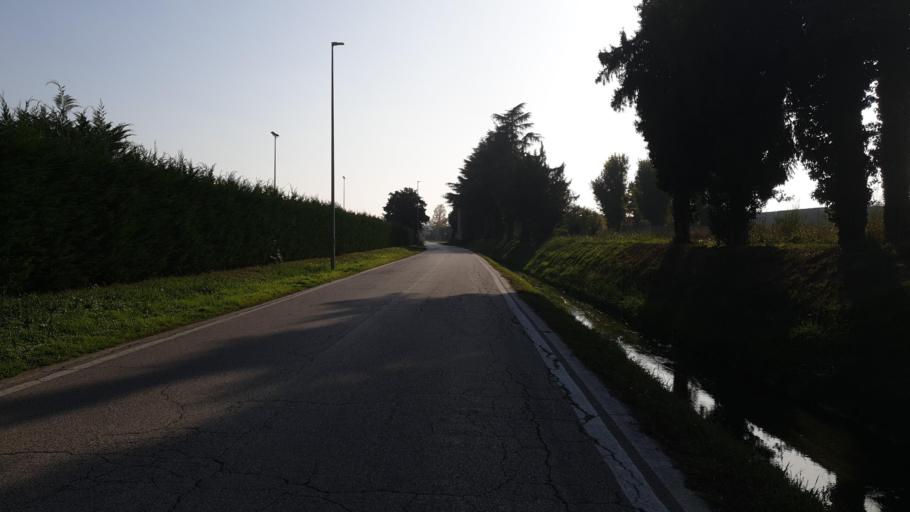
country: IT
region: Veneto
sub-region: Provincia di Padova
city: Oltre Brenta
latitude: 45.4017
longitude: 11.9973
